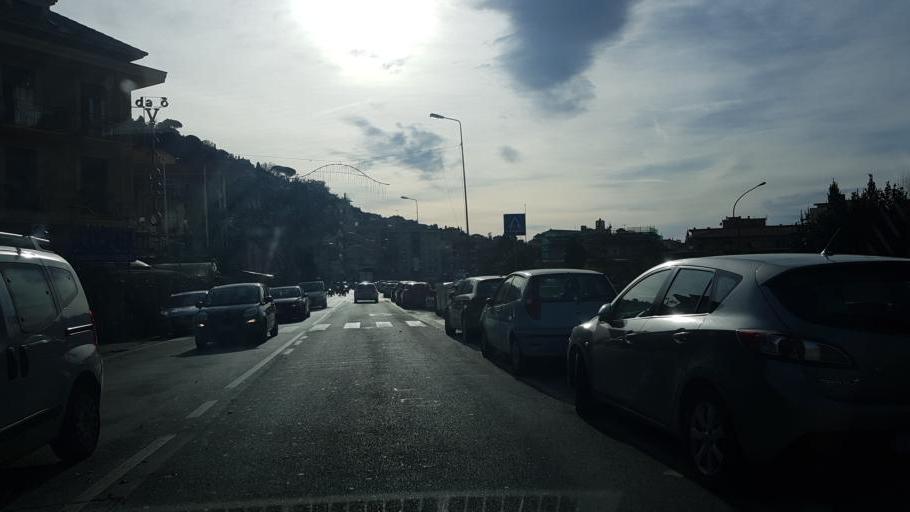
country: IT
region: Liguria
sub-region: Provincia di Genova
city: Recco
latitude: 44.3670
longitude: 9.1465
